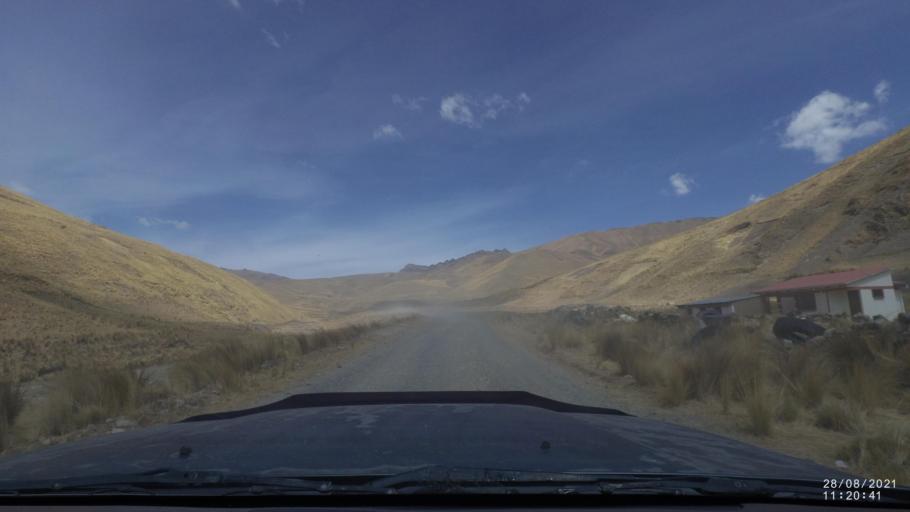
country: BO
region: Cochabamba
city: Sipe Sipe
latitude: -17.1602
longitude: -66.3423
